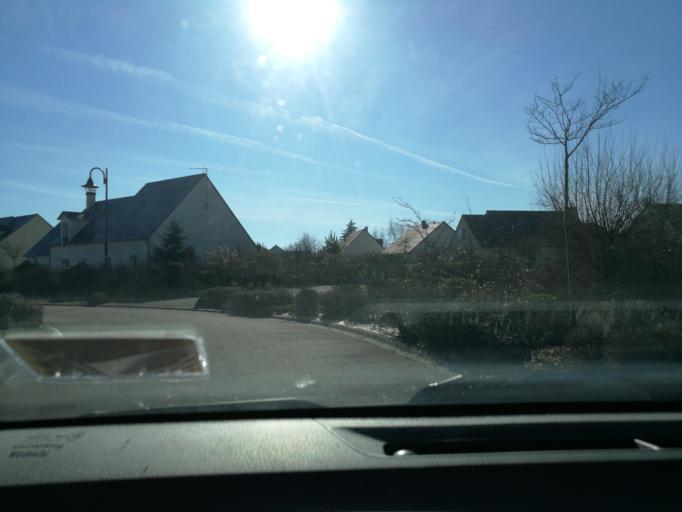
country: FR
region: Centre
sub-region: Departement du Loiret
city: Chaingy
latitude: 47.8843
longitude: 1.7790
